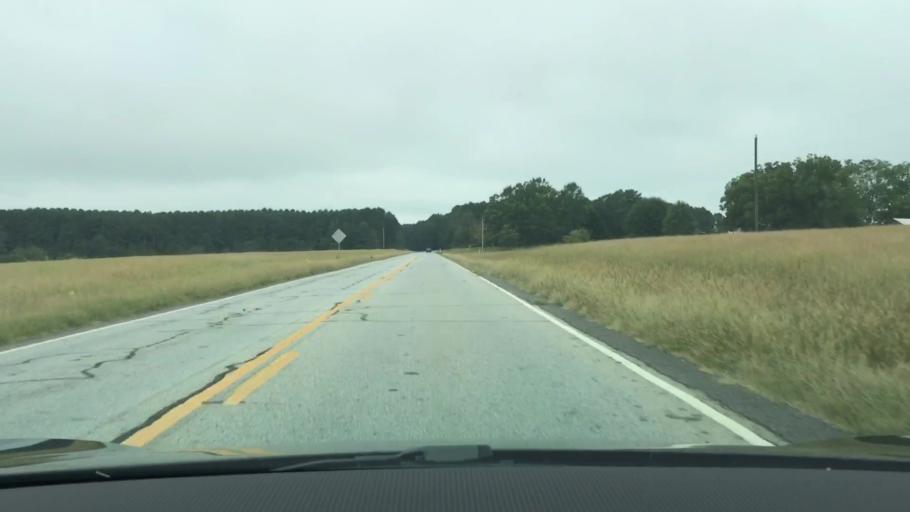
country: US
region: Georgia
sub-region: Barrow County
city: Russell
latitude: 33.9598
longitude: -83.6648
